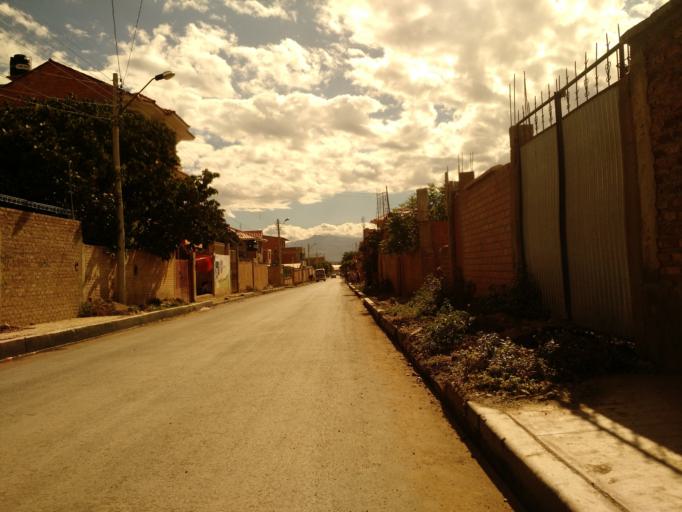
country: BO
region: Cochabamba
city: Cochabamba
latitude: -17.4585
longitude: -66.1514
